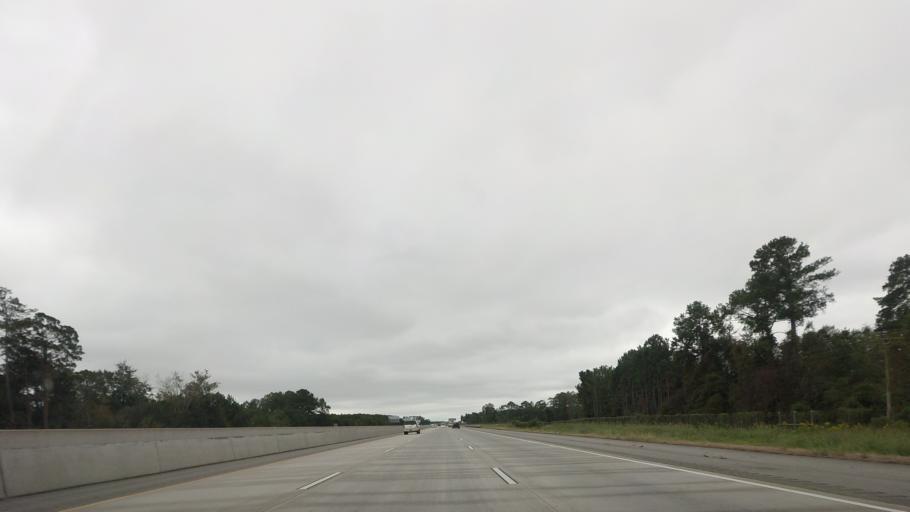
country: US
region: Georgia
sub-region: Cook County
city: Sparks
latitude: 31.2311
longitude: -83.4636
